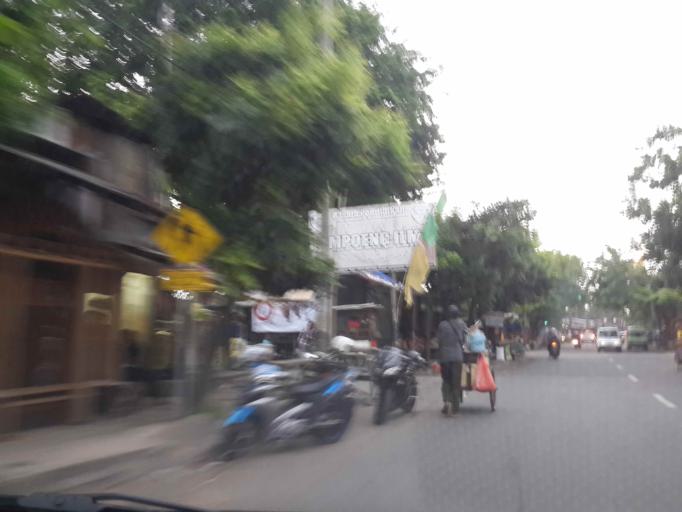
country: ID
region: East Java
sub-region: Kota Surabaya
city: Surabaya
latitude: -7.2522
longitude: 112.7290
